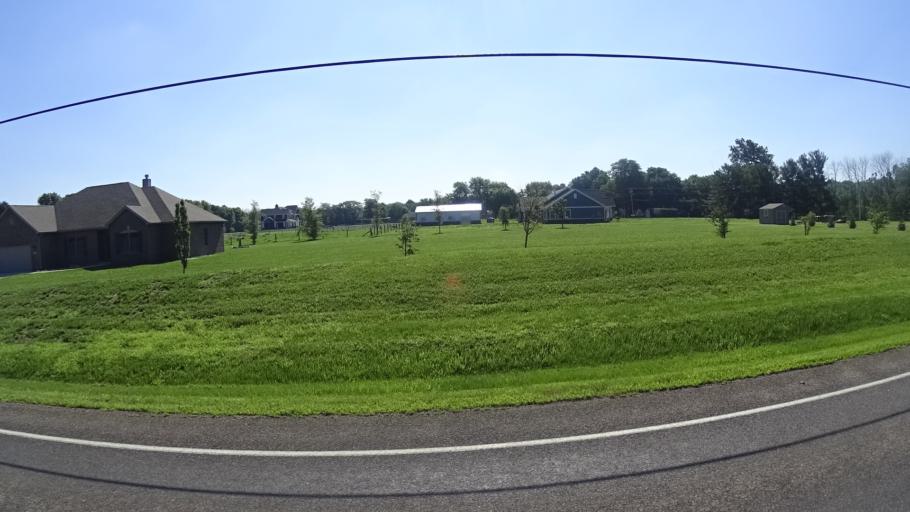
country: US
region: Indiana
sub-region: Hancock County
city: Fortville
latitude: 39.9602
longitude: -85.8432
